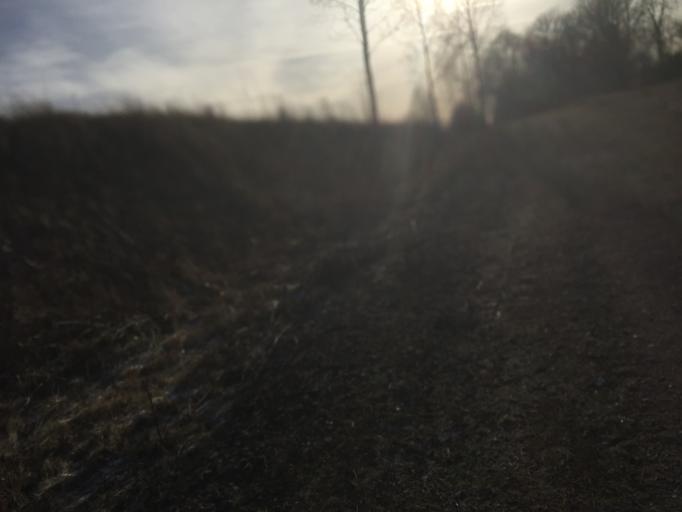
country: SE
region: Joenkoeping
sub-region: Aneby Kommun
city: Aneby
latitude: 57.8264
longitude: 14.8183
